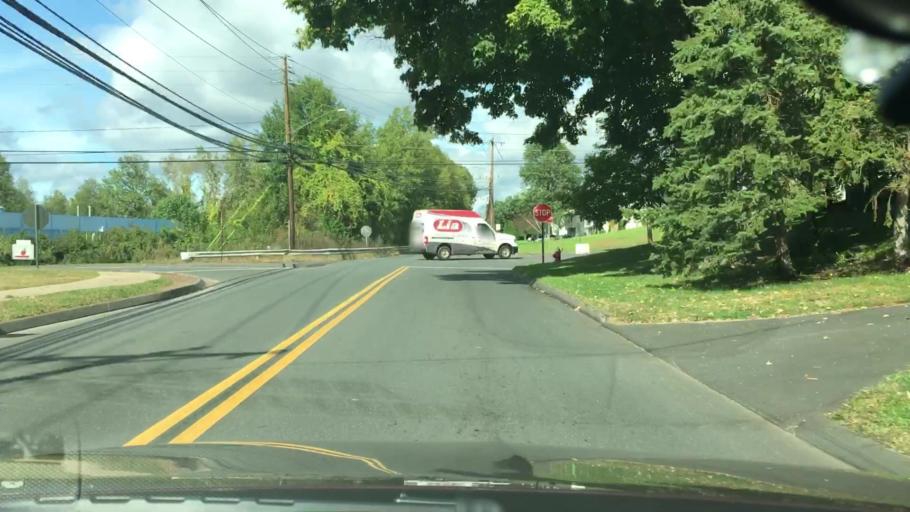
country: US
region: Connecticut
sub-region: Hartford County
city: Hazardville
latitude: 42.0048
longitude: -72.5134
